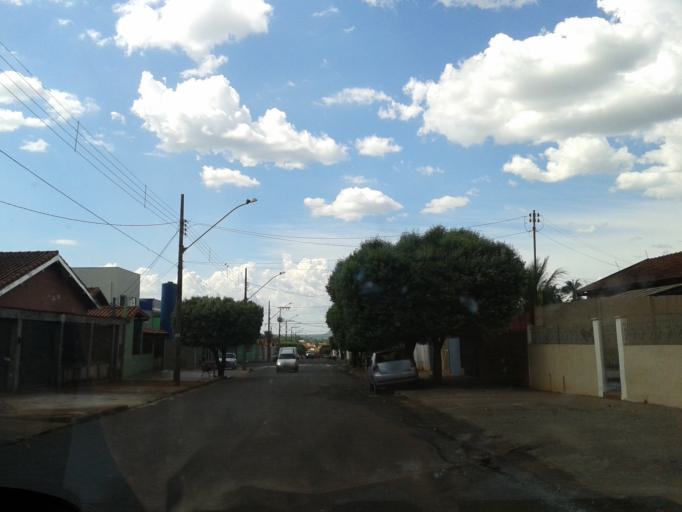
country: BR
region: Minas Gerais
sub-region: Ituiutaba
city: Ituiutaba
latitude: -18.9853
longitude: -49.4695
